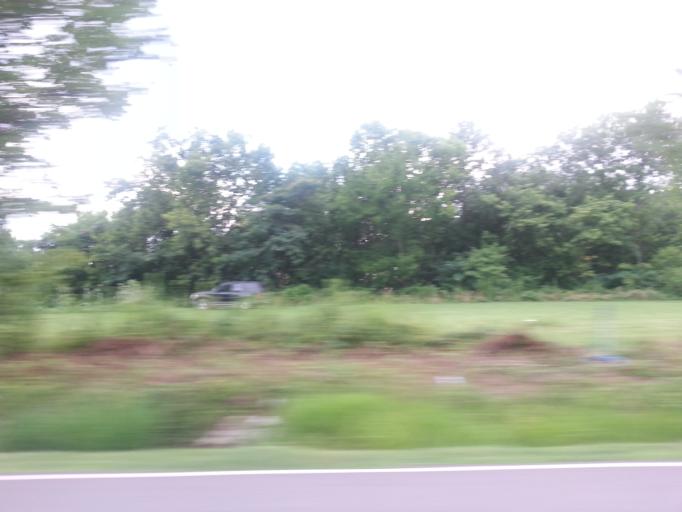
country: US
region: Tennessee
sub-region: Knox County
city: Knoxville
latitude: 36.0144
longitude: -83.9208
